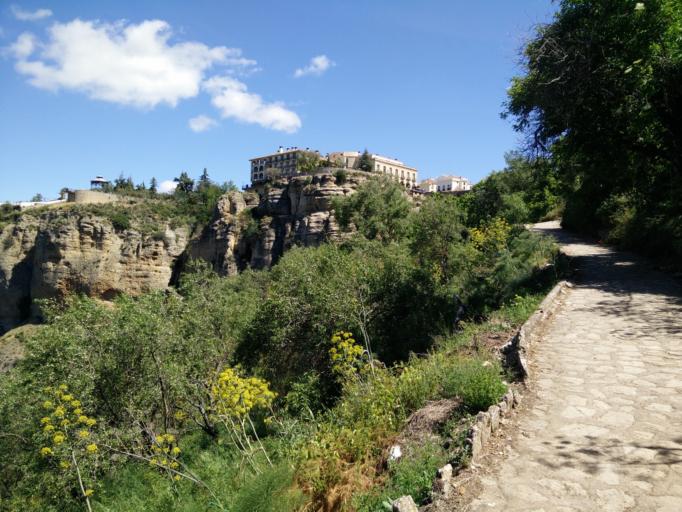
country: ES
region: Andalusia
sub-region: Provincia de Malaga
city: Ronda
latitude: 36.7388
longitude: -5.1675
